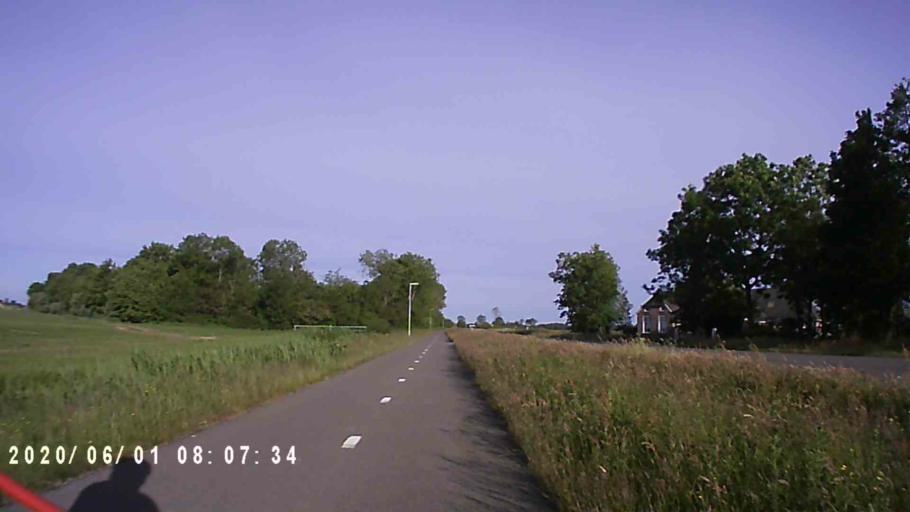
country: NL
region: Friesland
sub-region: Gemeente Ferwerderadiel
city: Burdaard
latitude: 53.2828
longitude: 5.9033
